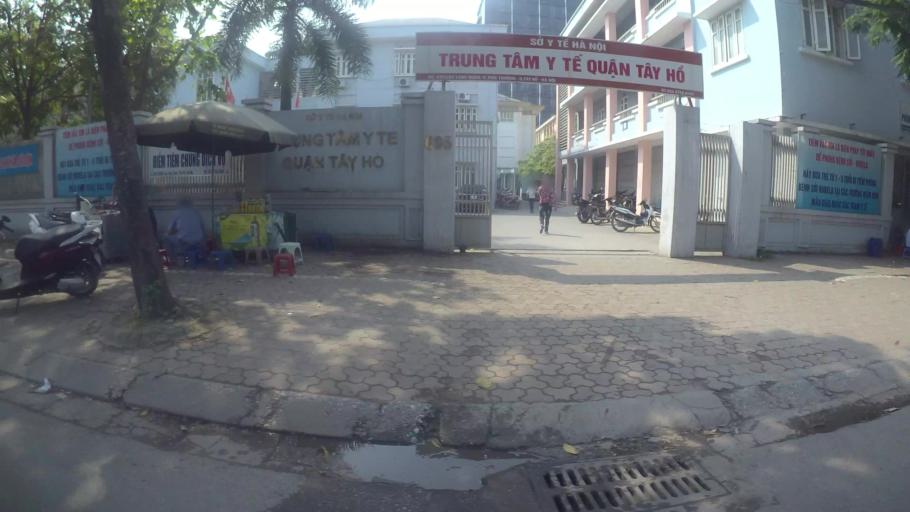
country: VN
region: Ha Noi
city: Tay Ho
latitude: 21.0796
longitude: 105.8166
